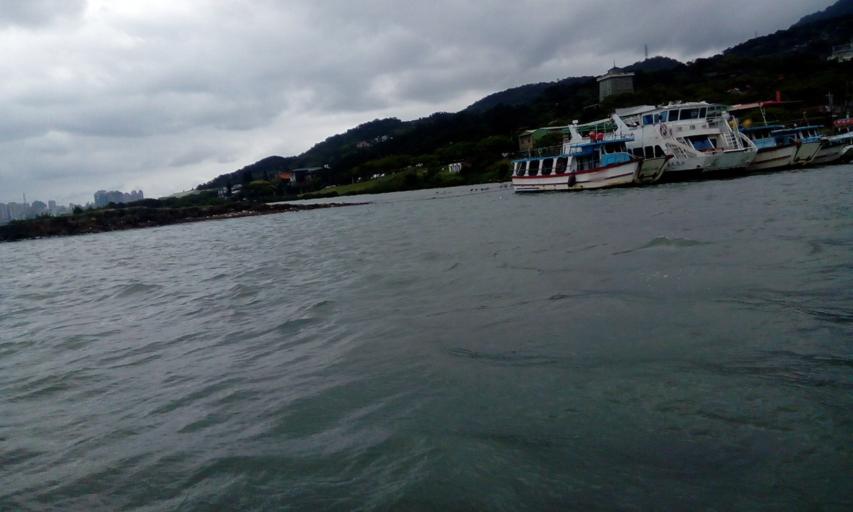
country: TW
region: Taipei
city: Taipei
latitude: 25.1597
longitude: 121.4361
